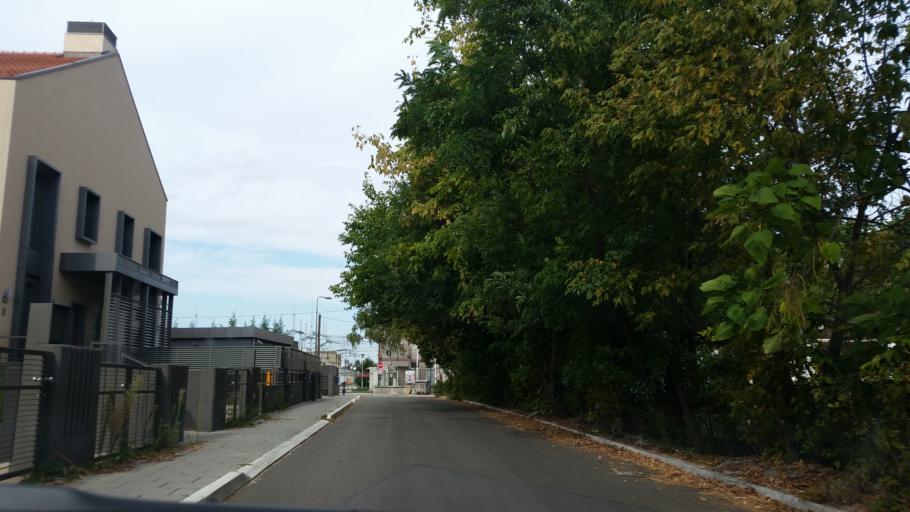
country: RS
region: Central Serbia
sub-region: Belgrade
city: Zemun
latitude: 44.8225
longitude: 20.3871
